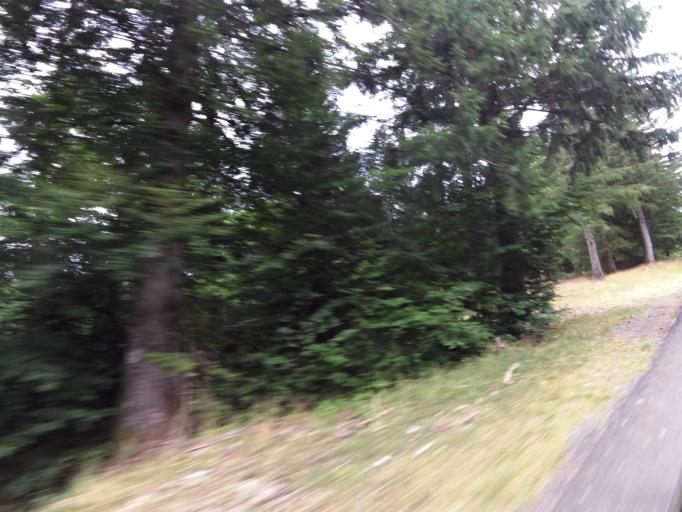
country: FR
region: Languedoc-Roussillon
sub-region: Departement du Gard
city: Valleraugue
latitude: 44.0860
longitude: 3.5620
